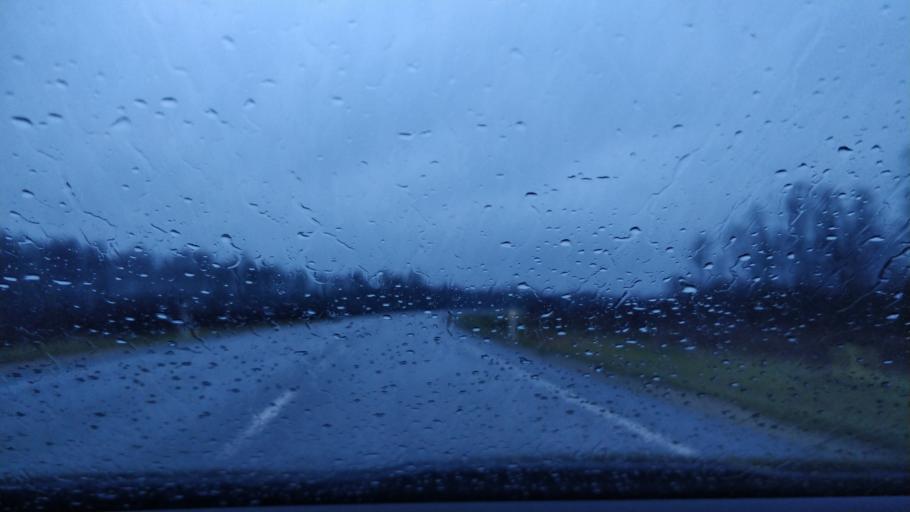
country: EE
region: Laeaene
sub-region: Lihula vald
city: Lihula
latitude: 58.7970
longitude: 24.0455
